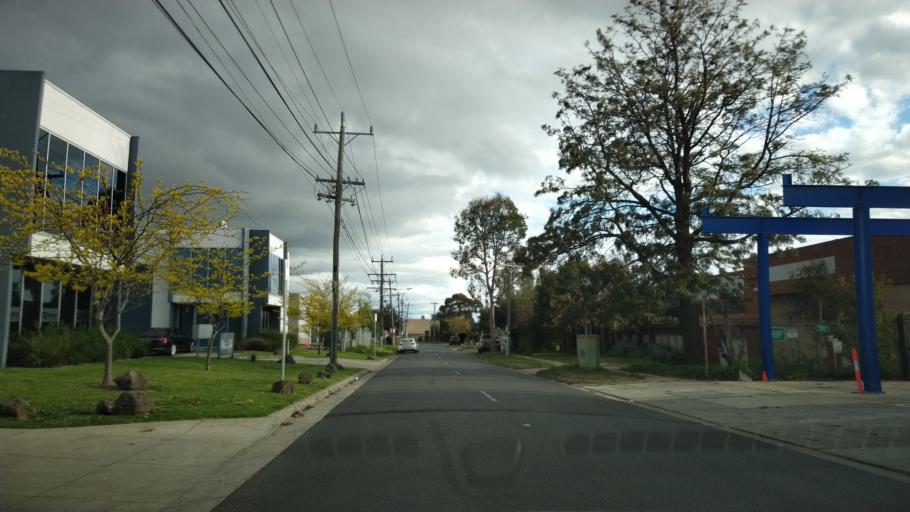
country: AU
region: Victoria
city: Highett
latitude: -37.9496
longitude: 145.0667
